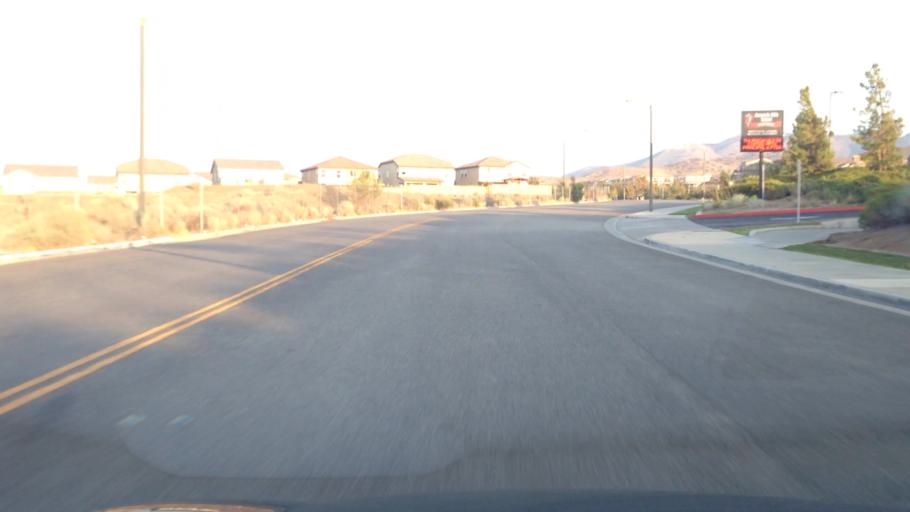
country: US
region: California
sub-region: Los Angeles County
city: Desert View Highlands
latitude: 34.5661
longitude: -118.1803
